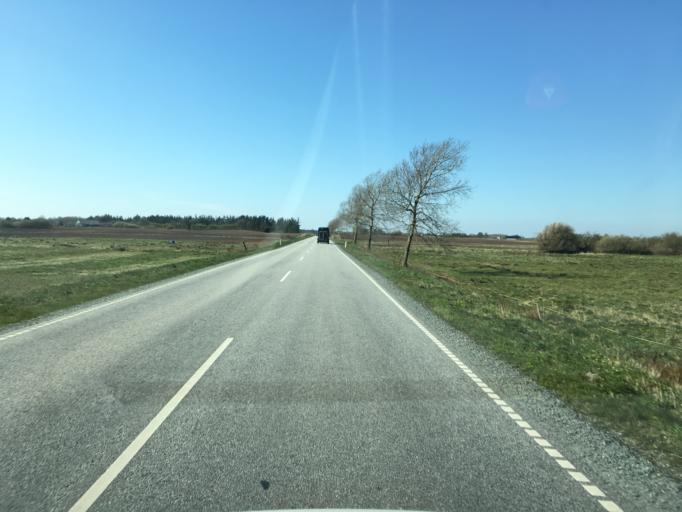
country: DK
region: South Denmark
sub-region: Aabenraa Kommune
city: Tinglev
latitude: 54.9602
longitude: 9.3291
